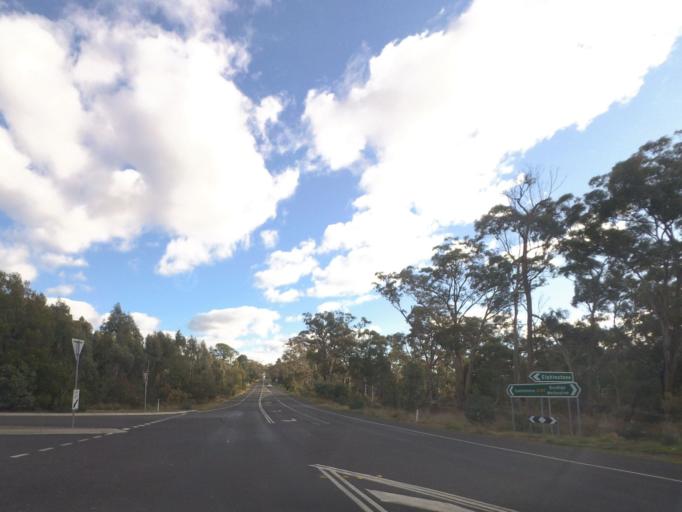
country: AU
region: Victoria
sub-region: Mount Alexander
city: Castlemaine
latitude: -37.1031
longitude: 144.3169
